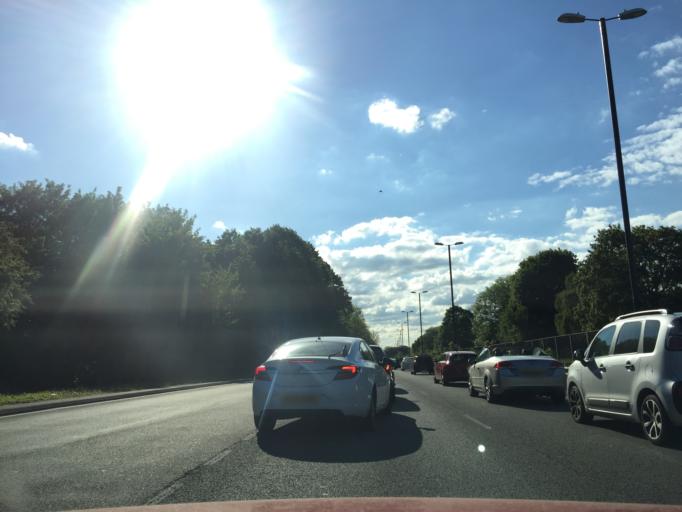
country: GB
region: England
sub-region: Coventry
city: Coventry
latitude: 52.3784
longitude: -1.5070
